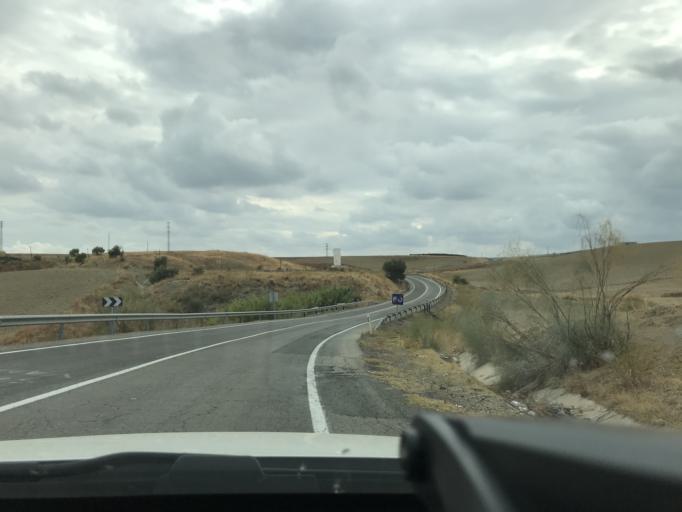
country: ES
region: Andalusia
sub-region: Provincia de Sevilla
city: Cantillana
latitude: 37.6194
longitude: -5.7917
